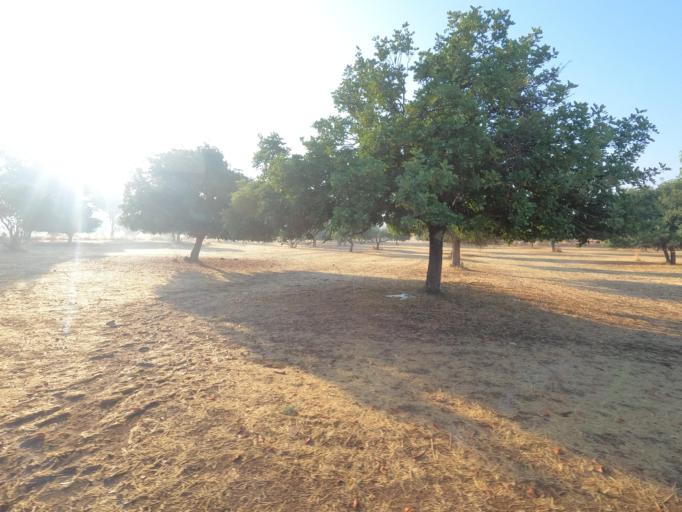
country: CY
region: Larnaka
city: Mosfiloti
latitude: 34.9752
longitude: 33.4340
